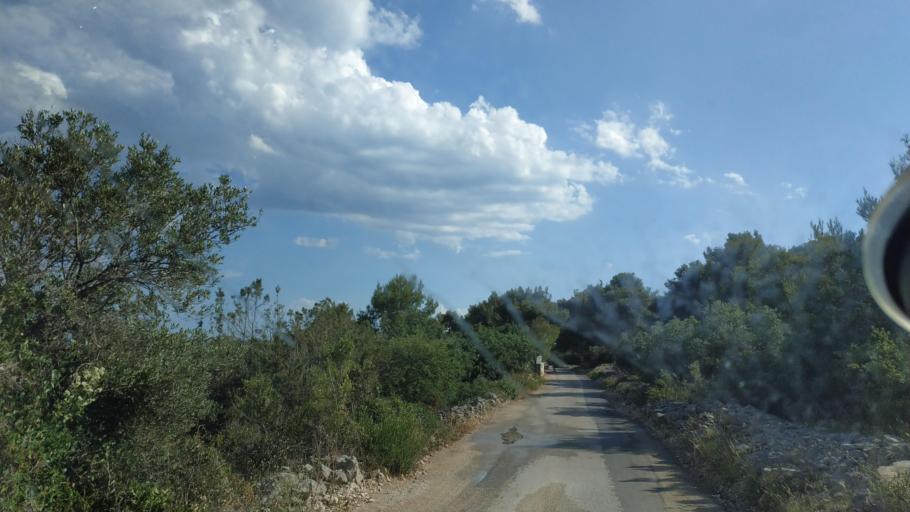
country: HR
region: Splitsko-Dalmatinska
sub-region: Grad Trogir
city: Trogir
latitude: 43.4852
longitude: 16.2451
